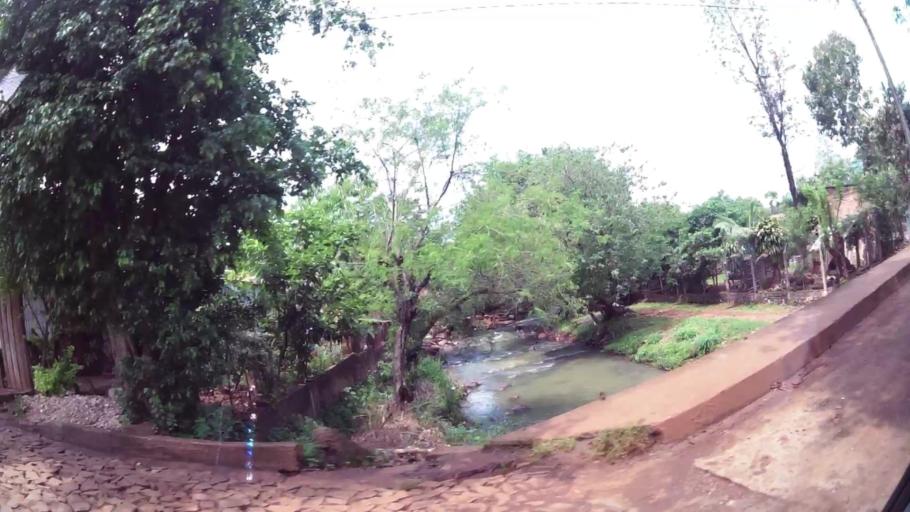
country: PY
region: Alto Parana
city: Ciudad del Este
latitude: -25.5002
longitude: -54.6261
